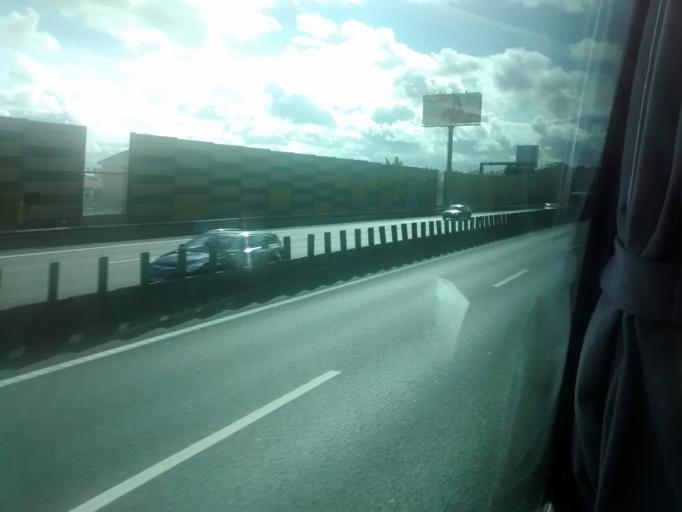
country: PT
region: Lisbon
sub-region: Loures
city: Bobadela
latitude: 38.8099
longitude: -9.1030
